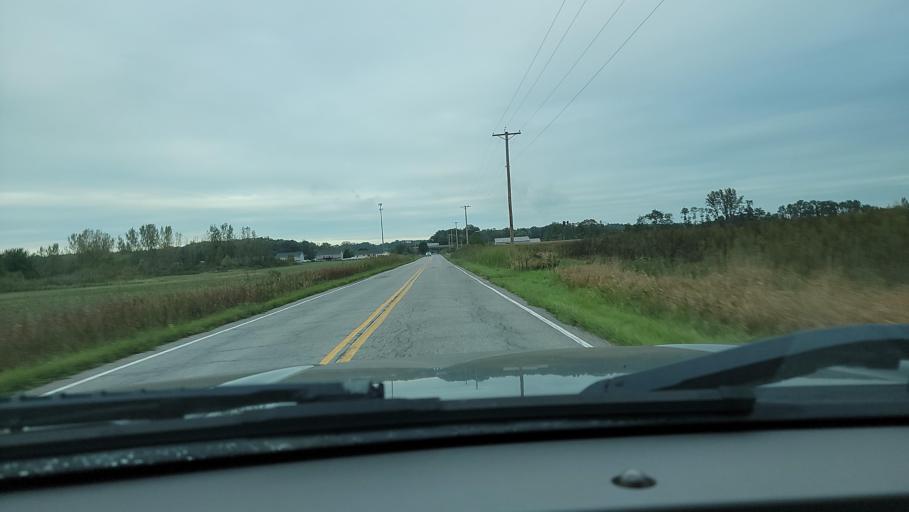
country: US
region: Indiana
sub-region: Porter County
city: Portage
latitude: 41.5686
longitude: -87.1533
